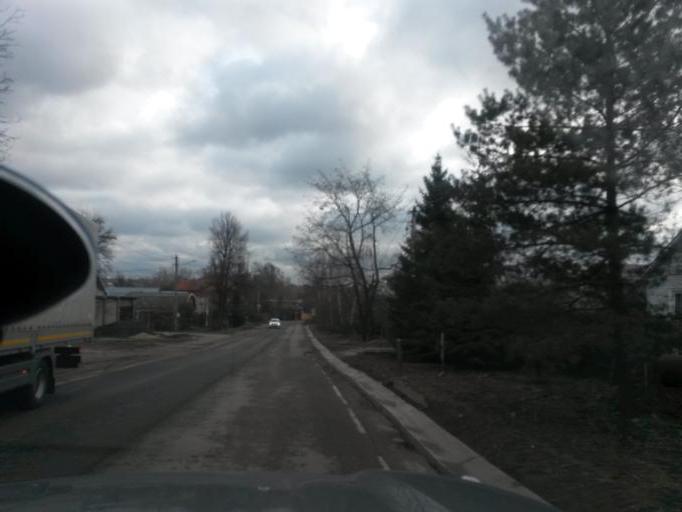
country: RU
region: Moscow
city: Zyablikovo
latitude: 55.6142
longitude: 37.7855
